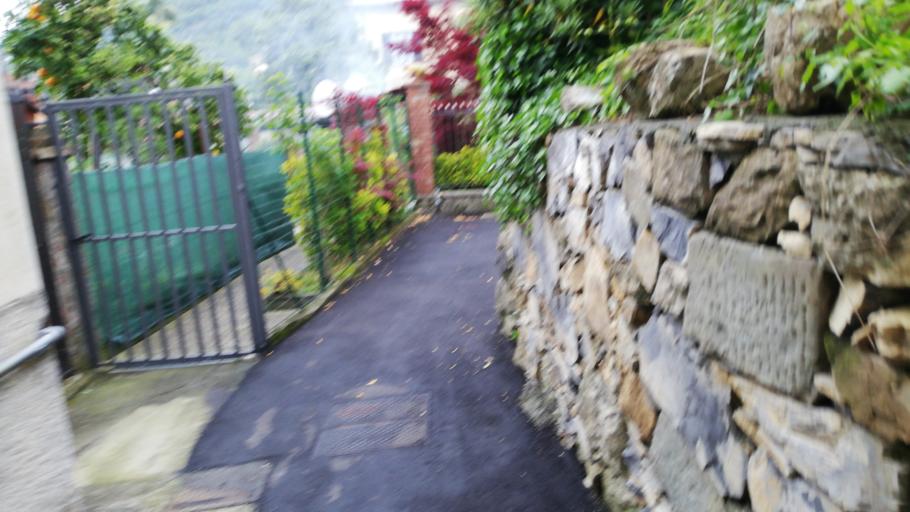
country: IT
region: Liguria
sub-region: Provincia di Genova
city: Piccarello
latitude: 44.4515
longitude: 9.0109
